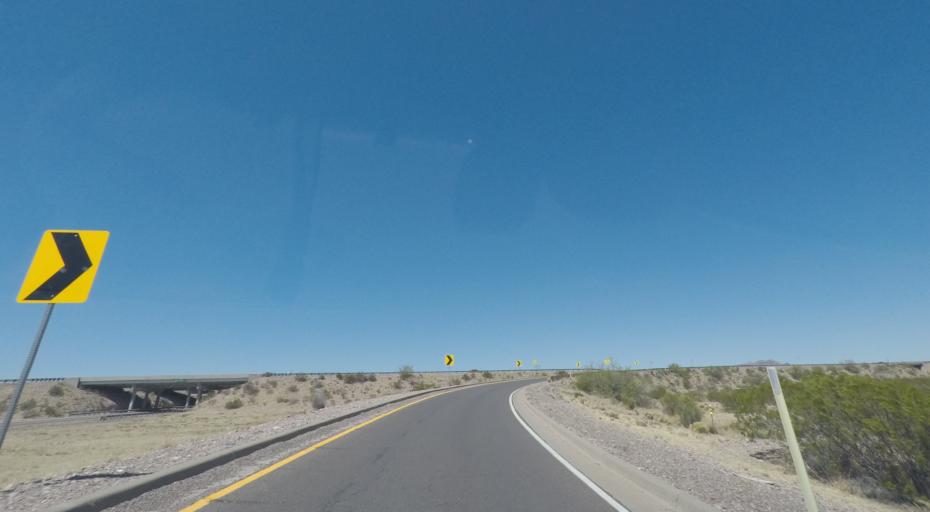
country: US
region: New Mexico
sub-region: Socorro County
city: Socorro
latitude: 33.9179
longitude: -106.8774
